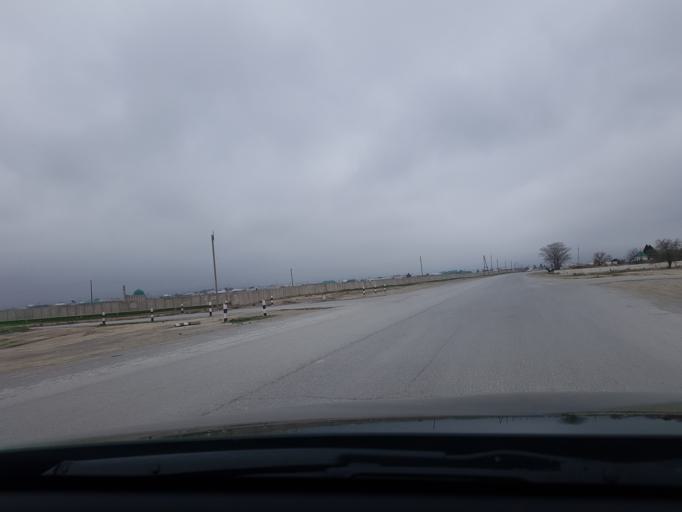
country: TM
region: Ahal
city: Arcabil
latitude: 38.1351
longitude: 57.9476
